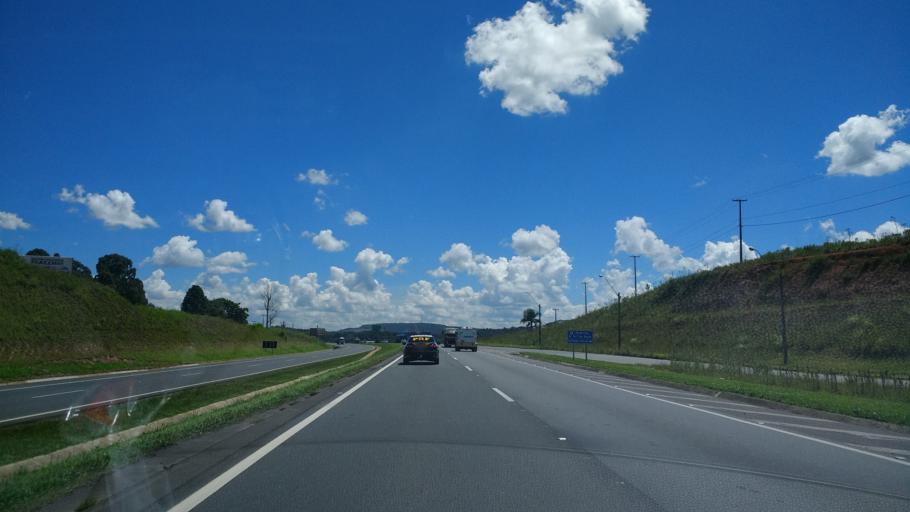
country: BR
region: Parana
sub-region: Campo Largo
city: Campo Largo
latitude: -25.4412
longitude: -49.5588
